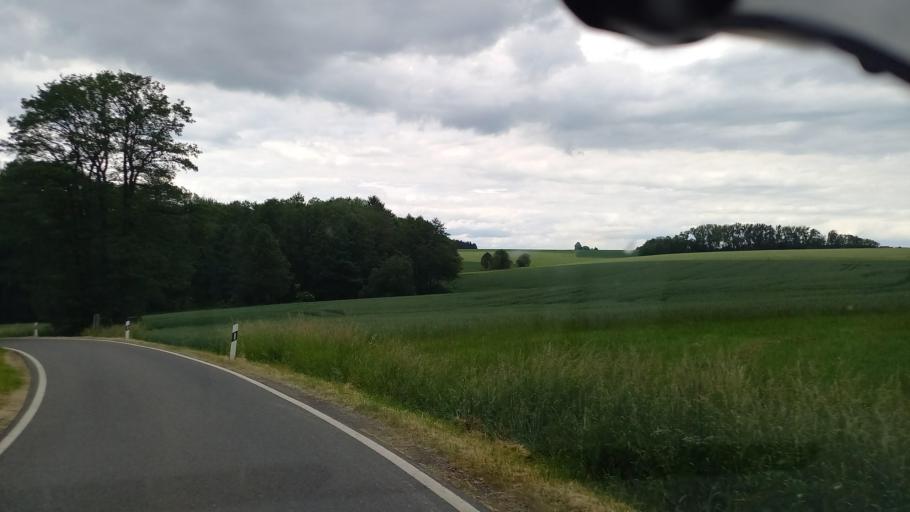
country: DE
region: Saxony
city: Hirschfeld
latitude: 50.6339
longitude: 12.4253
